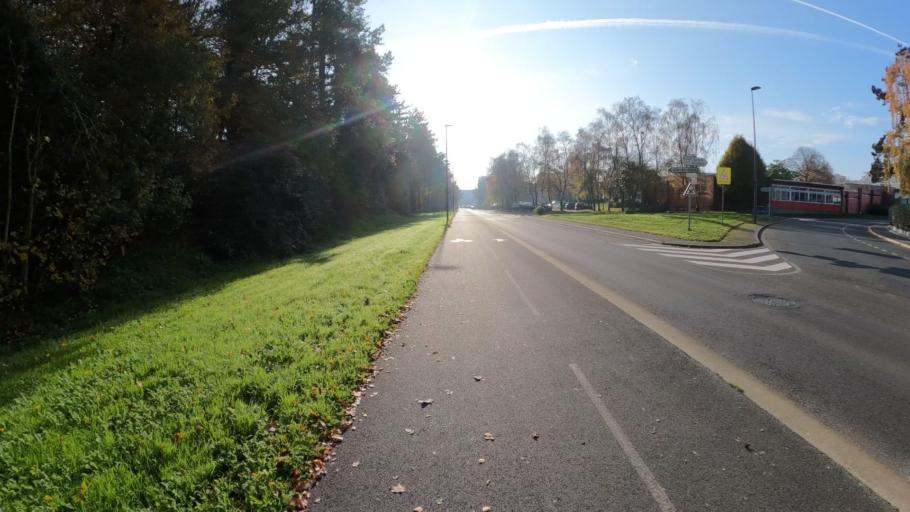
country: FR
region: Lower Normandy
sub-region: Departement du Calvados
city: Herouville-Saint-Clair
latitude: 49.2071
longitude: -0.3349
